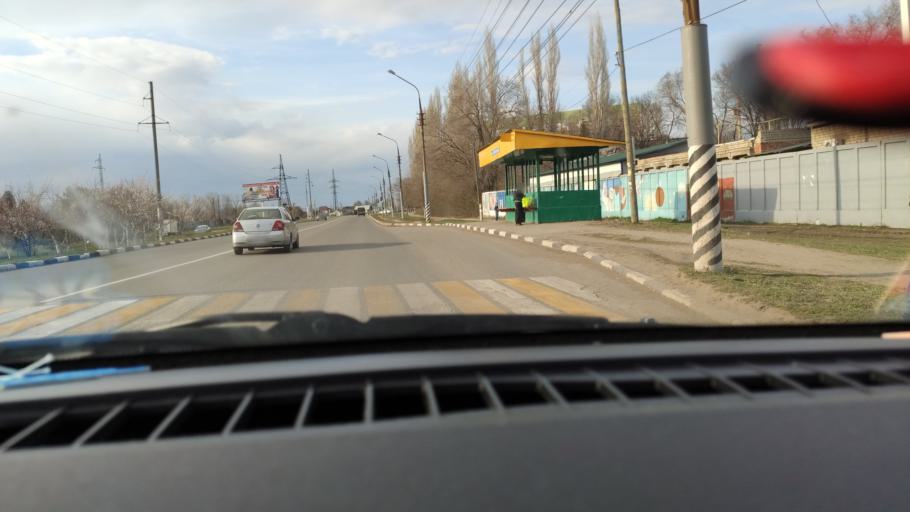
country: RU
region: Saratov
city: Privolzhskiy
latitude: 51.3959
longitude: 46.0342
